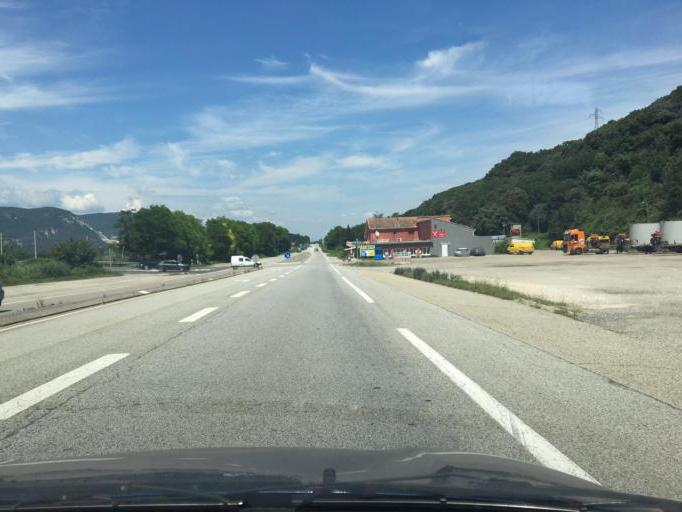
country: FR
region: Rhone-Alpes
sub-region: Departement de la Drome
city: Savasse
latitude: 44.6027
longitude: 4.7536
